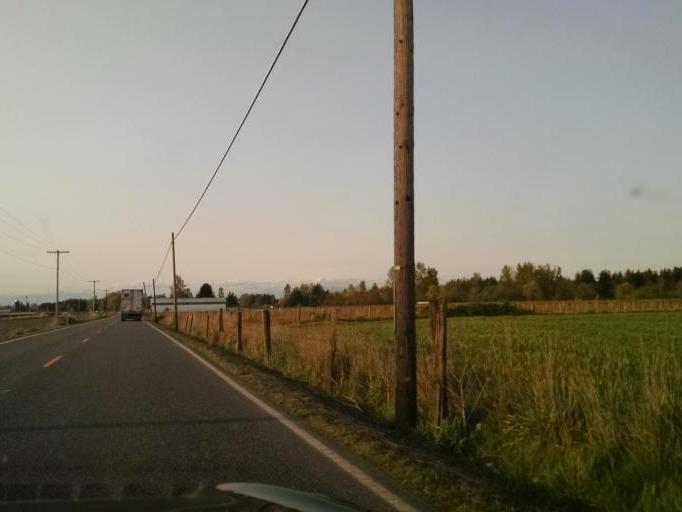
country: US
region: Washington
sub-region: Whatcom County
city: Nooksack
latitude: 48.9014
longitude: -122.3206
